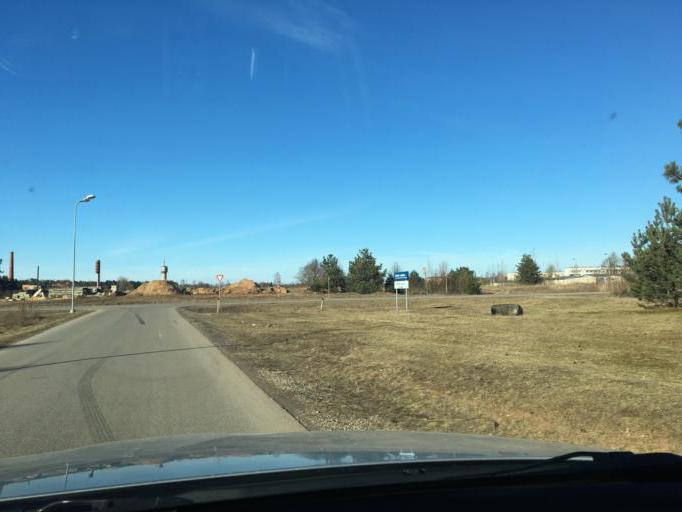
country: LV
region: Jekabpils Rajons
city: Jekabpils
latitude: 56.4859
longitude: 25.8499
